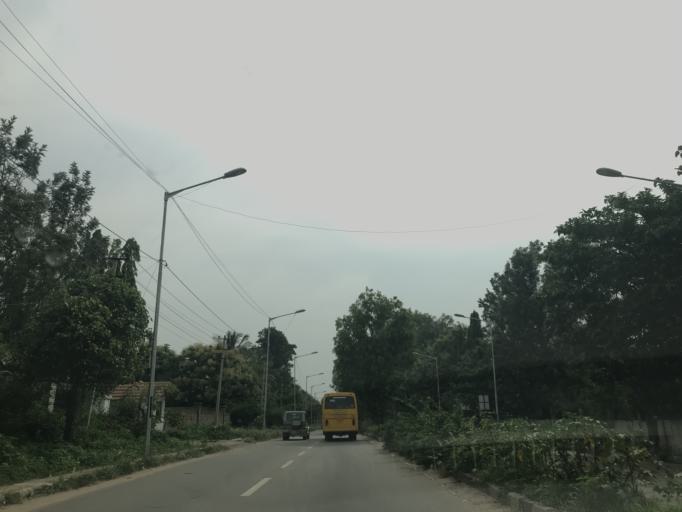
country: IN
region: Karnataka
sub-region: Bangalore Urban
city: Yelahanka
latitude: 13.1229
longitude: 77.6357
